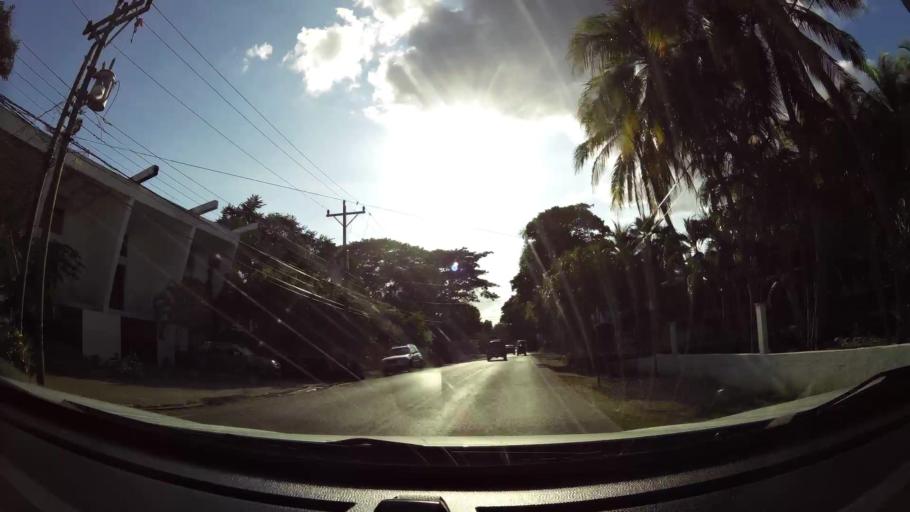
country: CR
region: Guanacaste
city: Sardinal
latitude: 10.5519
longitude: -85.6941
